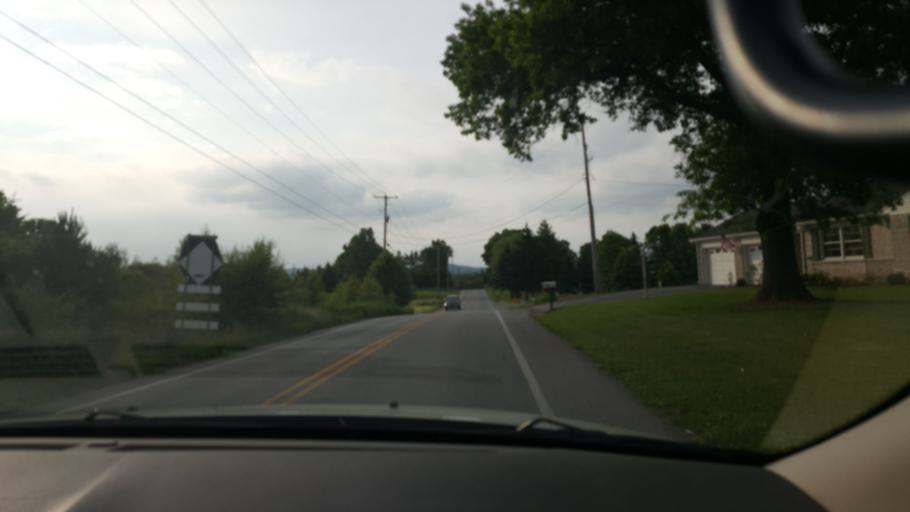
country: US
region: Pennsylvania
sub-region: York County
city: Shiloh
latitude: 39.9957
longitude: -76.7947
